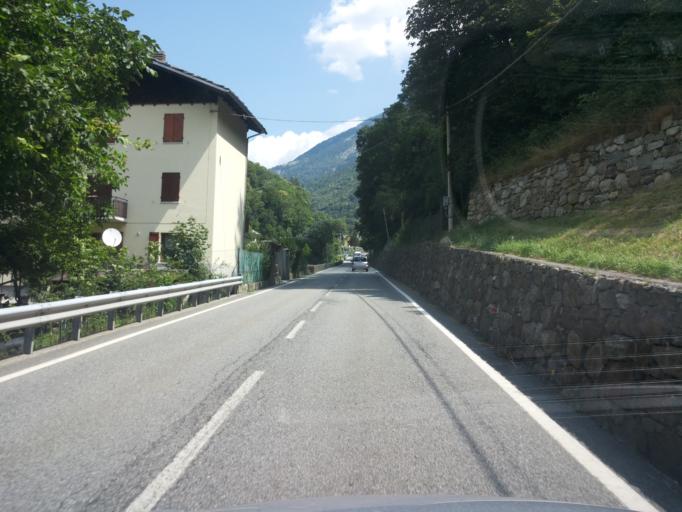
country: IT
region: Aosta Valley
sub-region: Valle d'Aosta
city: Fontainemore
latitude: 45.6435
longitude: 7.8565
